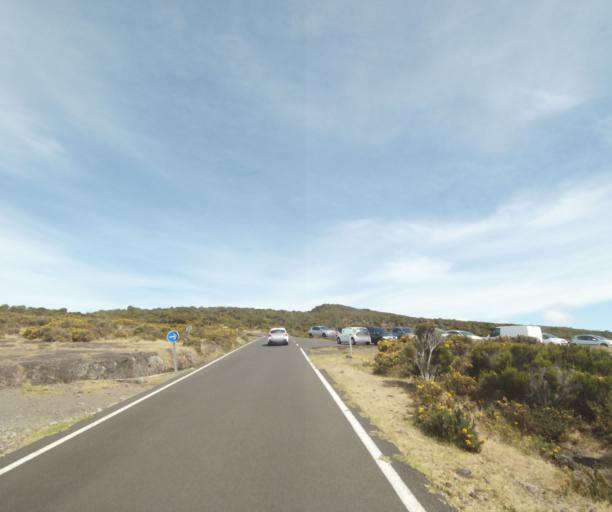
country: RE
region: Reunion
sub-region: Reunion
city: Trois-Bassins
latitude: -21.0713
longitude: 55.3864
